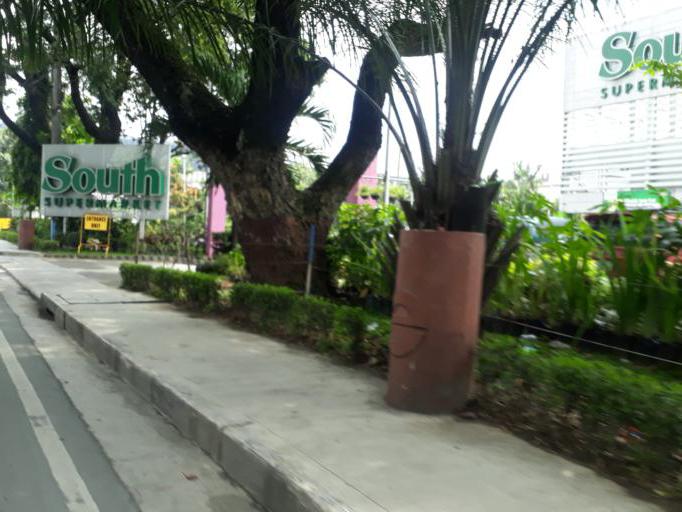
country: PH
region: Metro Manila
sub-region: Marikina
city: Calumpang
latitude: 14.6167
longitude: 121.0925
